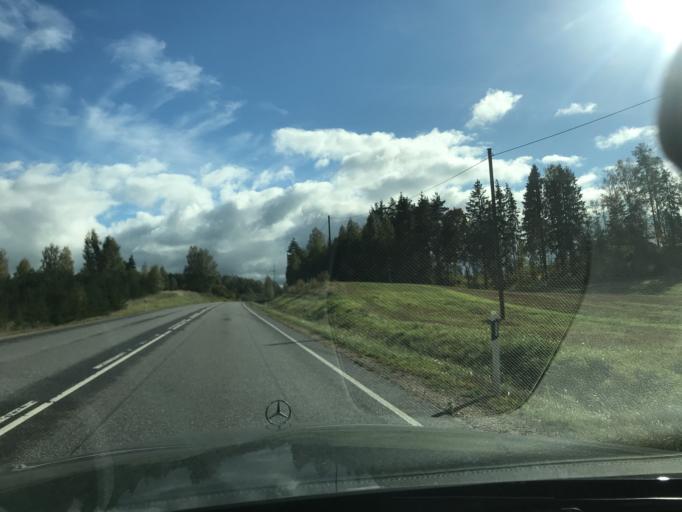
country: EE
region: Vorumaa
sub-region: Voru linn
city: Voru
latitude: 57.8055
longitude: 27.0788
